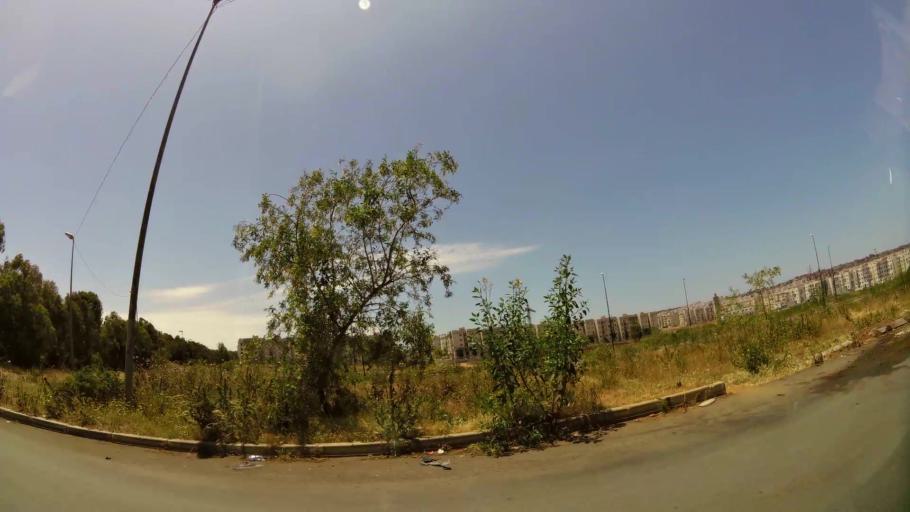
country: MA
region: Gharb-Chrarda-Beni Hssen
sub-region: Kenitra Province
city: Kenitra
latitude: 34.2521
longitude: -6.6334
